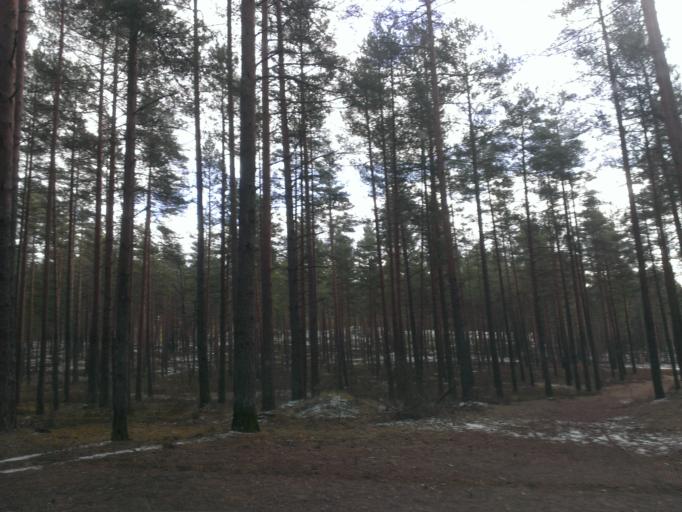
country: LV
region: Garkalne
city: Garkalne
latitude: 56.9651
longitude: 24.4333
